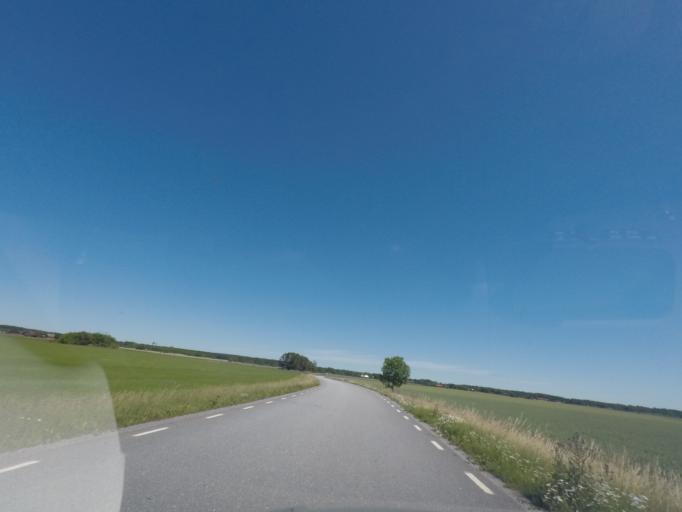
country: SE
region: Uppsala
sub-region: Enkopings Kommun
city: Enkoping
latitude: 59.7074
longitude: 17.0414
